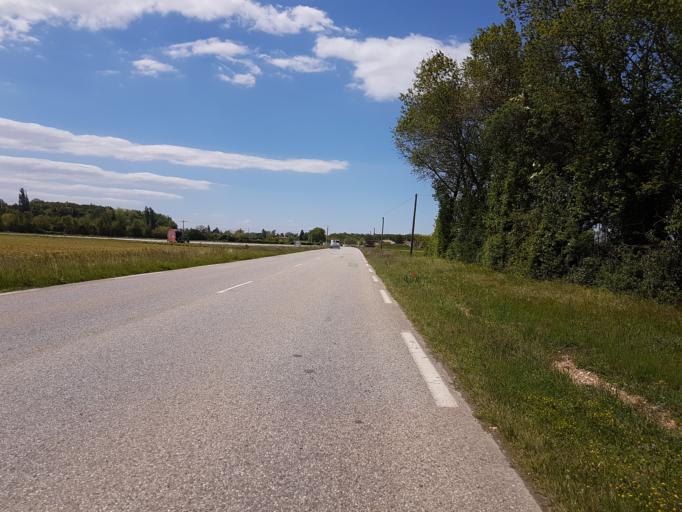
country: FR
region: Rhone-Alpes
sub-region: Departement de l'Isere
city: Saint-Romain-de-Jalionas
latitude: 45.7639
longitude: 5.2363
